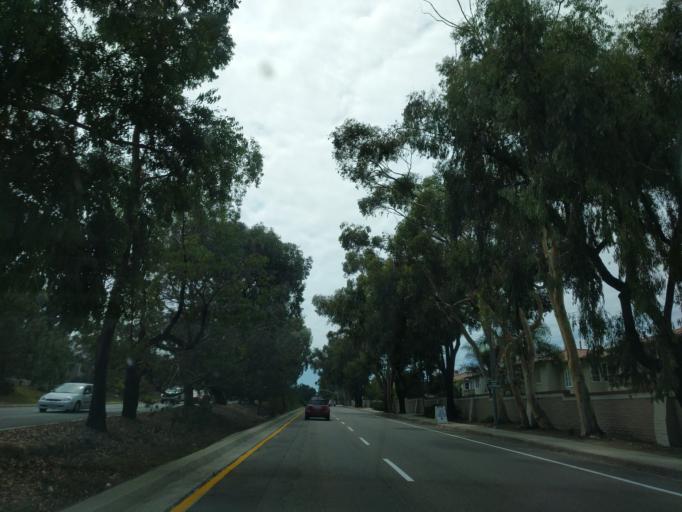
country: US
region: California
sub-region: San Diego County
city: La Jolla
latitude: 32.8831
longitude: -117.2439
